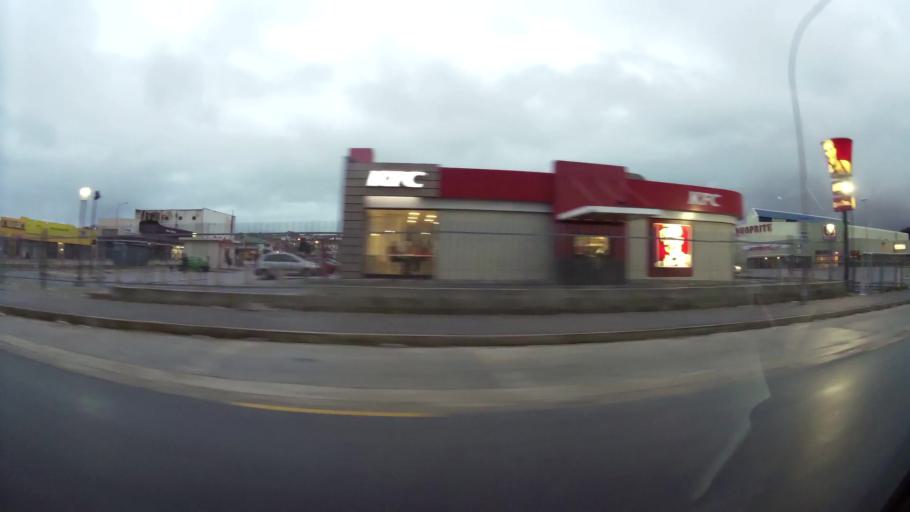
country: ZA
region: Eastern Cape
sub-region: Nelson Mandela Bay Metropolitan Municipality
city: Port Elizabeth
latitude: -33.9265
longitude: 25.5711
